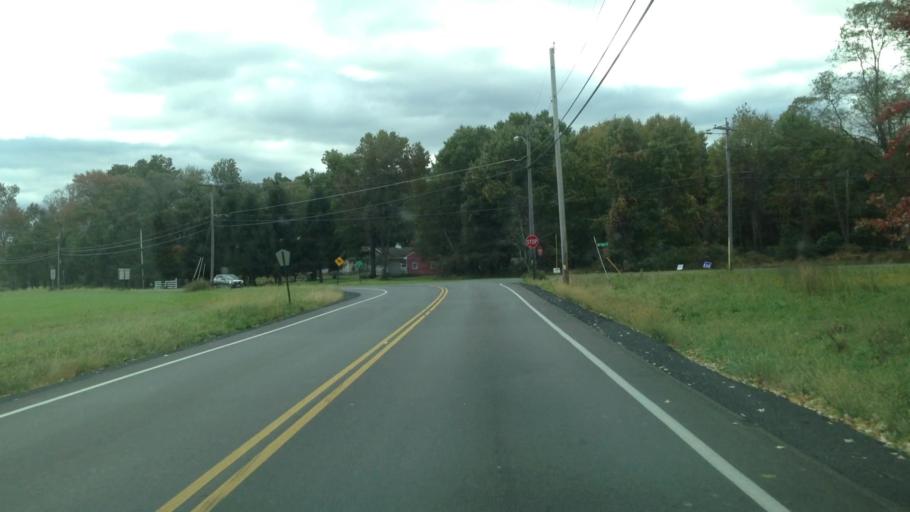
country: US
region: New York
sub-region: Ulster County
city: New Paltz
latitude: 41.7530
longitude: -74.0981
